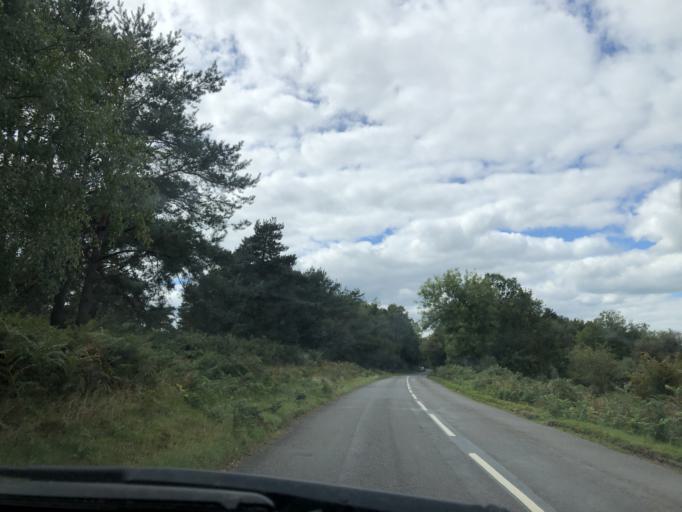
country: GB
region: England
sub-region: East Sussex
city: Forest Row
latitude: 51.0731
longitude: 0.0522
